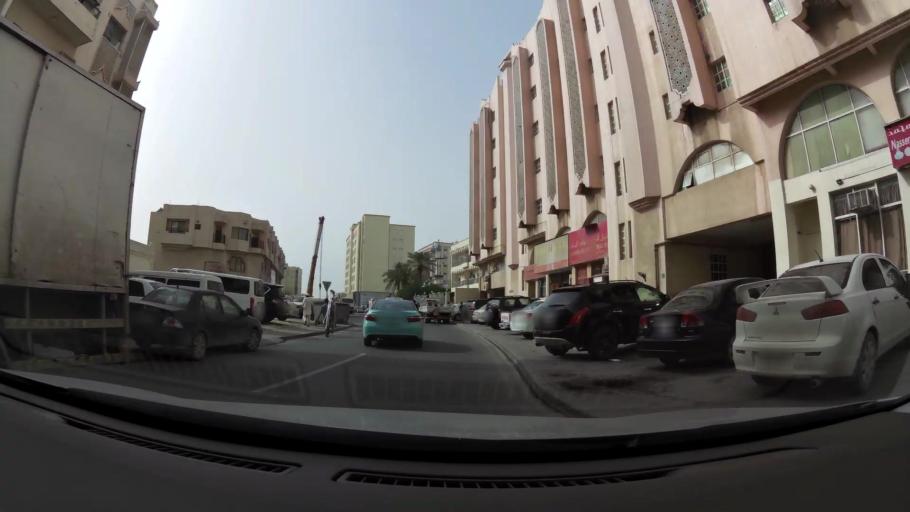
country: QA
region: Baladiyat ad Dawhah
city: Doha
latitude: 25.2797
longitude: 51.5474
